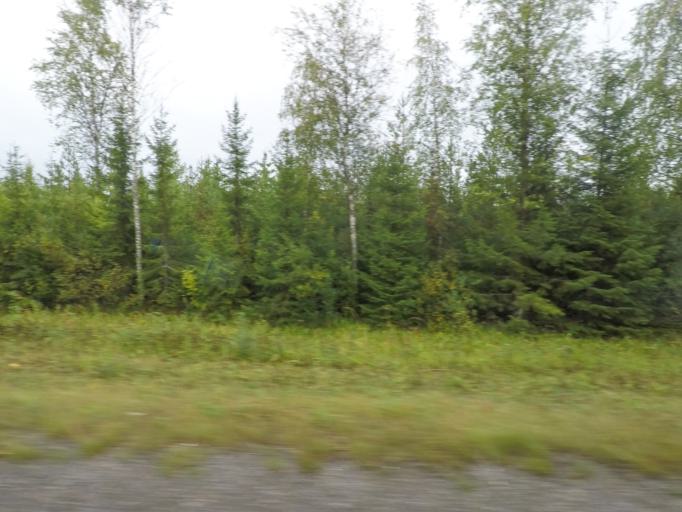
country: FI
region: Southern Savonia
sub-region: Pieksaemaeki
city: Joroinen
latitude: 62.1045
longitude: 27.8337
